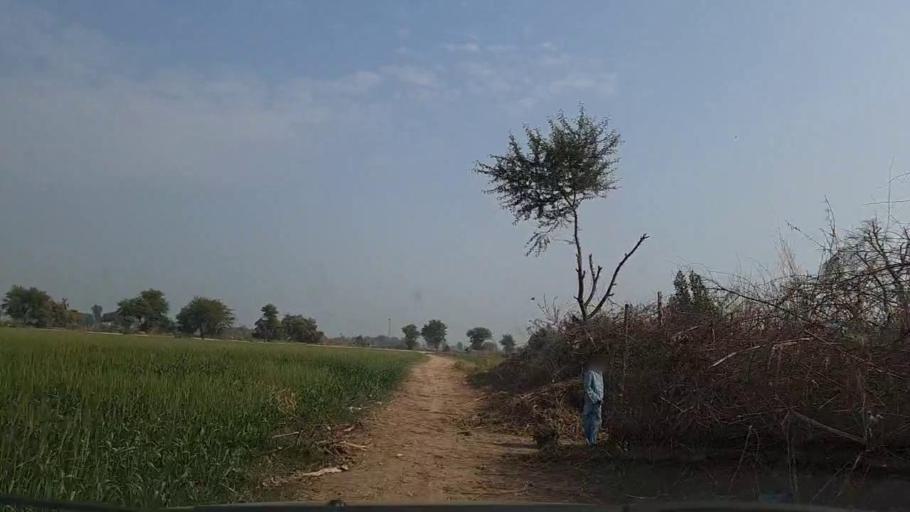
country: PK
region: Sindh
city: Sanghar
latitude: 26.0488
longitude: 68.9755
